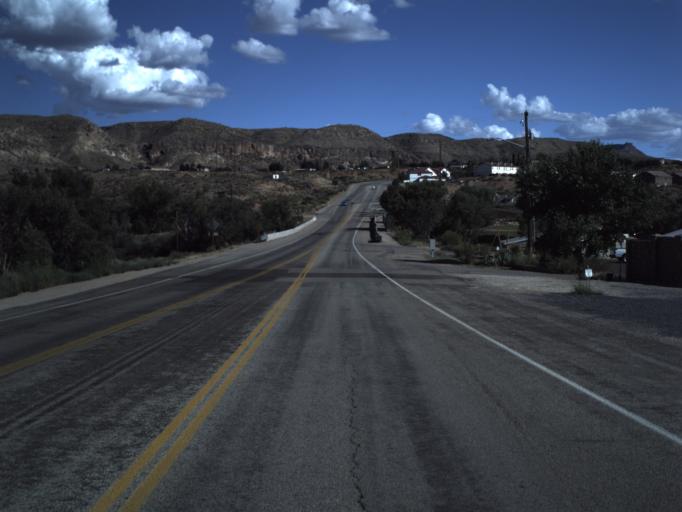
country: US
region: Utah
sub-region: Washington County
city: LaVerkin
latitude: 37.2207
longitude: -113.2772
